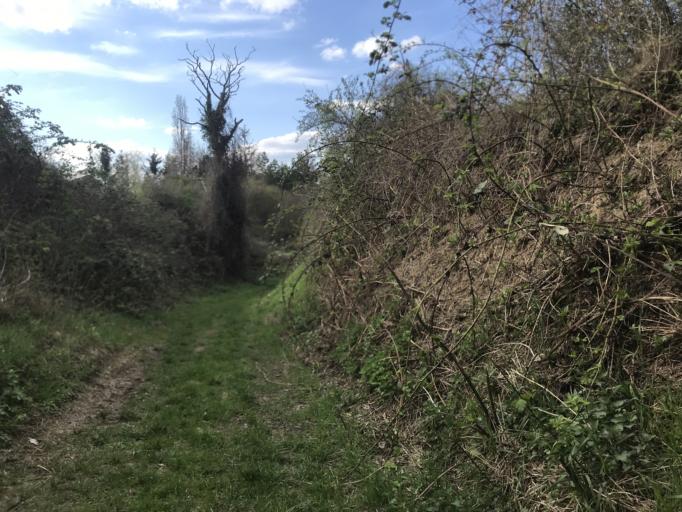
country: DE
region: Rheinland-Pfalz
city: Wackernheim
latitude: 49.9871
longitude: 8.1205
